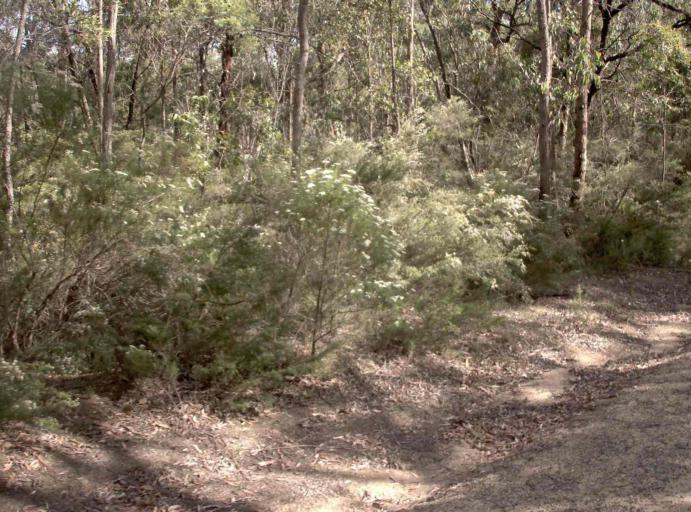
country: AU
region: Victoria
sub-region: East Gippsland
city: Lakes Entrance
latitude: -37.5504
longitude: 148.1476
